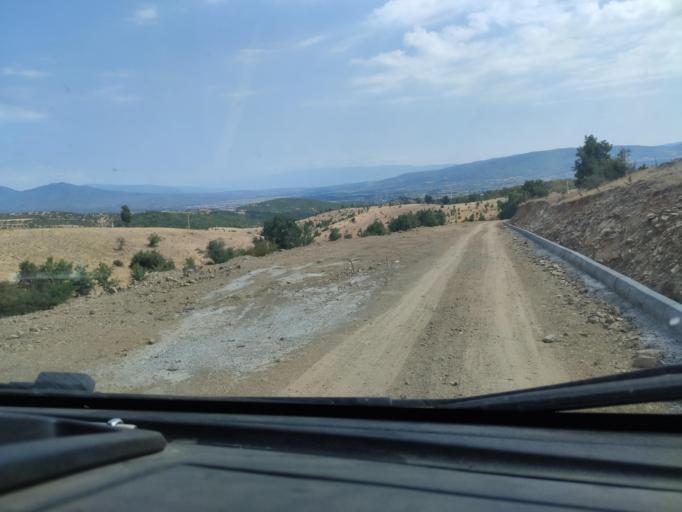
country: MK
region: Radovis
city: Radovish
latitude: 41.6718
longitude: 22.4045
